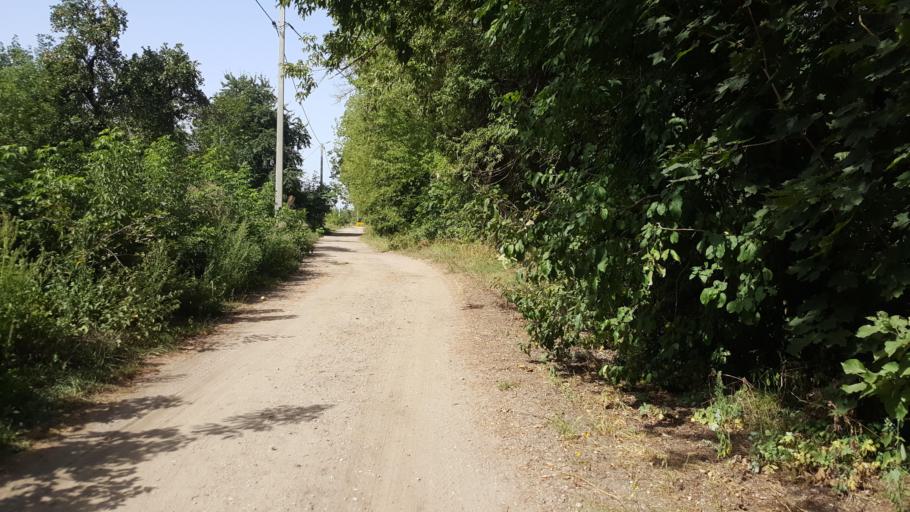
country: BY
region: Brest
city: Pruzhany
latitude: 52.4921
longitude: 24.6120
